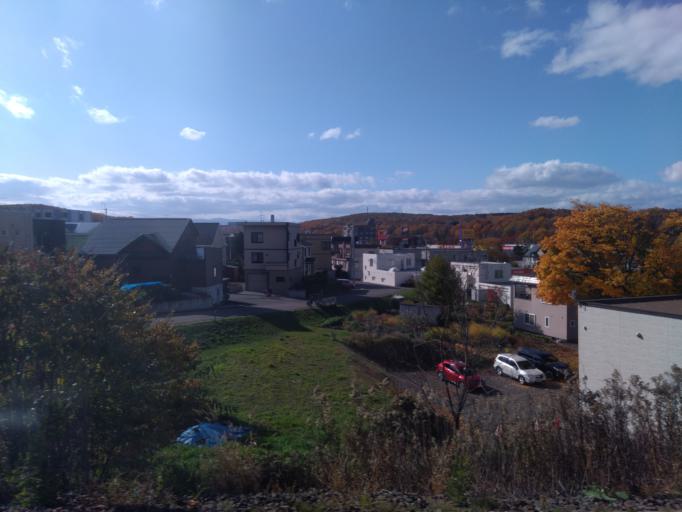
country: JP
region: Hokkaido
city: Kitahiroshima
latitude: 42.9847
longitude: 141.5623
